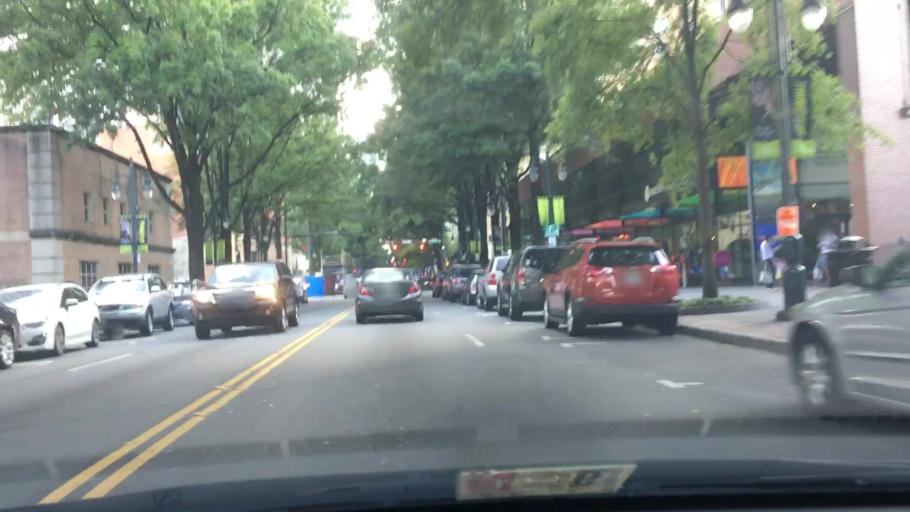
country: US
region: North Carolina
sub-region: Mecklenburg County
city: Charlotte
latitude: 35.2294
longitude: -80.8400
